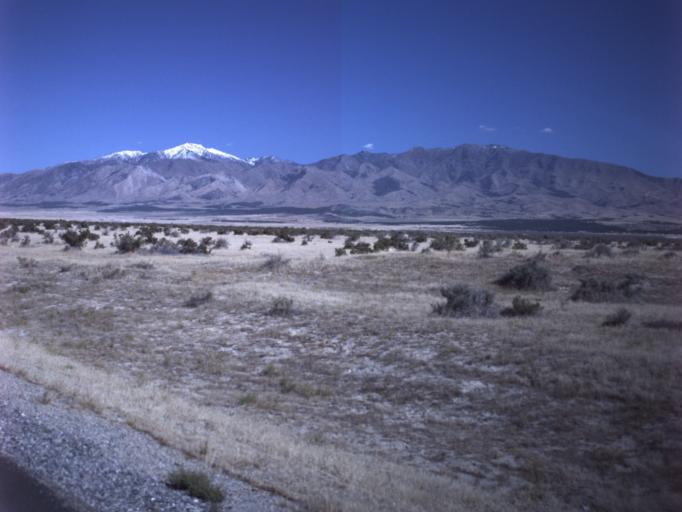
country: US
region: Utah
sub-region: Tooele County
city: Grantsville
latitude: 40.2765
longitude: -112.7416
